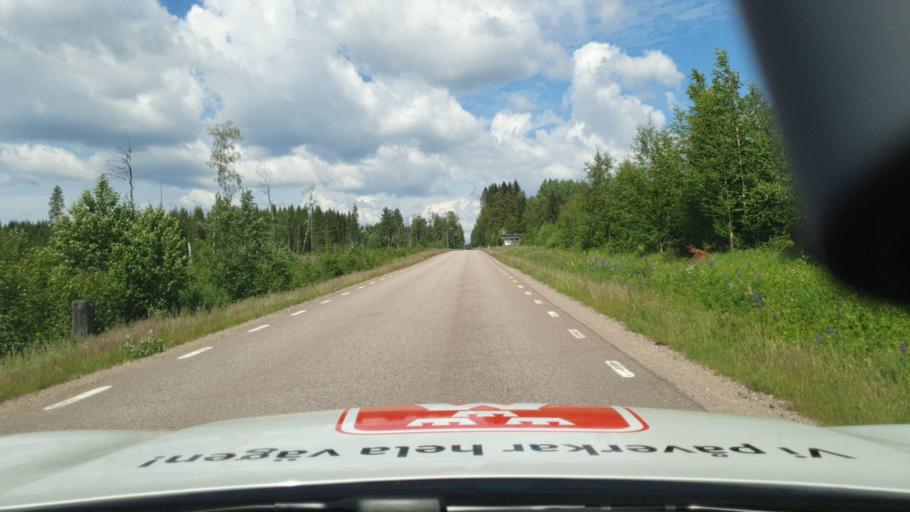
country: SE
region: Vaermland
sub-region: Torsby Kommun
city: Torsby
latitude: 60.4601
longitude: 12.8846
